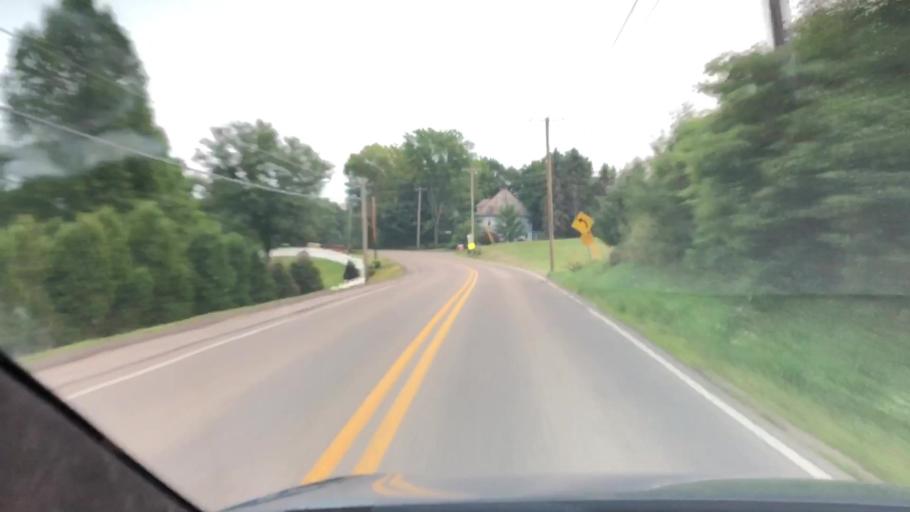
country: US
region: Pennsylvania
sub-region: Butler County
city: Shanor-Northvue
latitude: 40.8963
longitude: -79.9286
